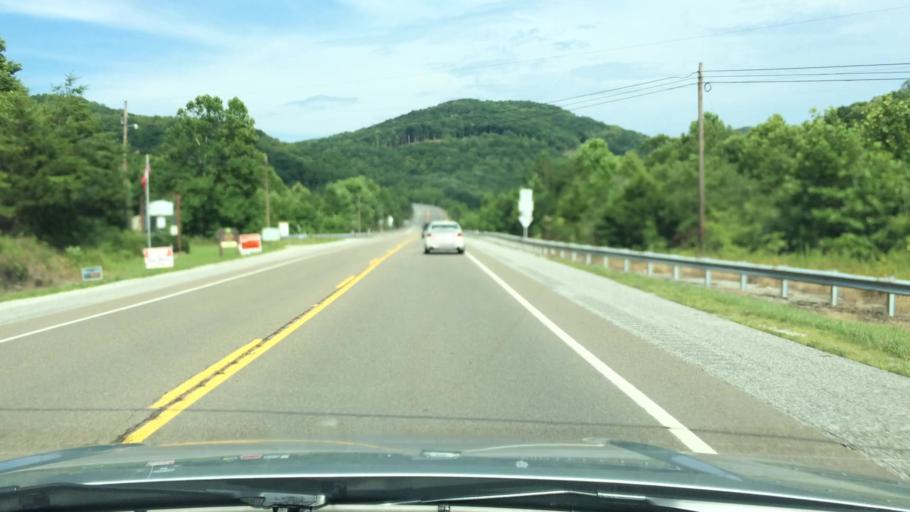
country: US
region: Tennessee
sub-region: Campbell County
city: Caryville
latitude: 36.3933
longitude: -84.3298
